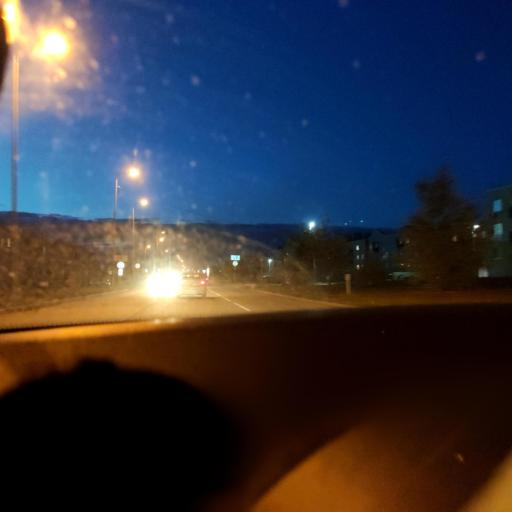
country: RU
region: Samara
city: Petra-Dubrava
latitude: 53.3103
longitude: 50.3093
